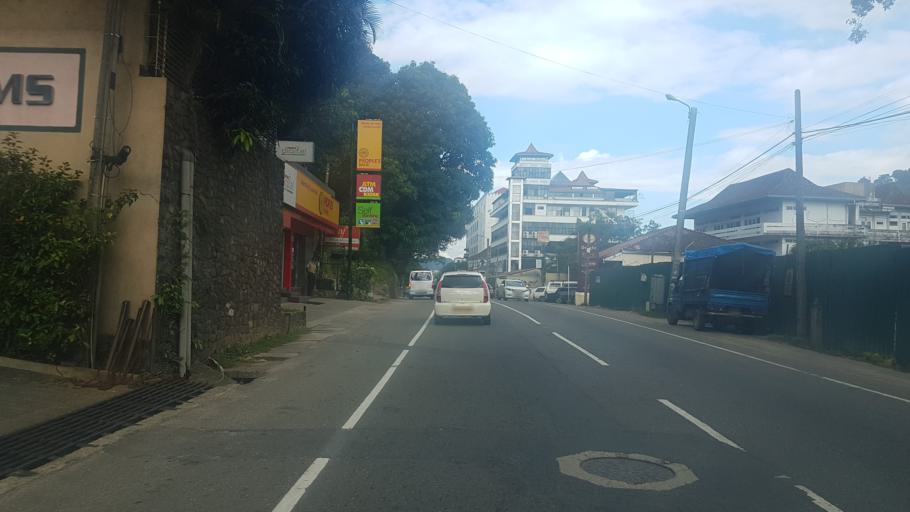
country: LK
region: Central
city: Kandy
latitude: 7.2758
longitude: 80.6137
